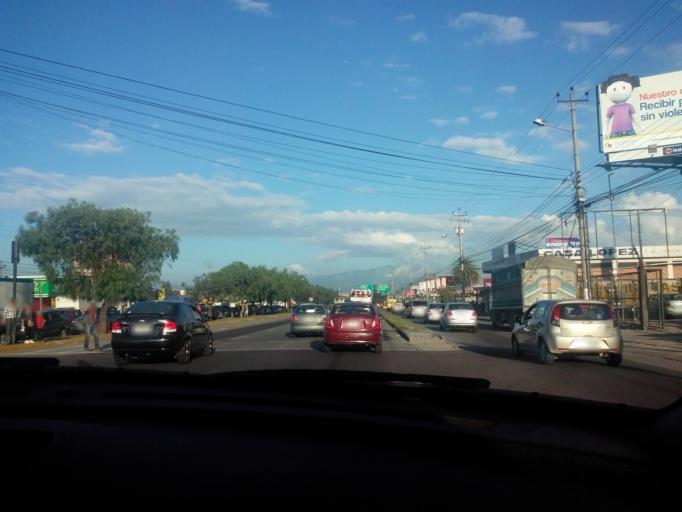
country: EC
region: Pichincha
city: Quito
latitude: -0.1087
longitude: -78.4540
